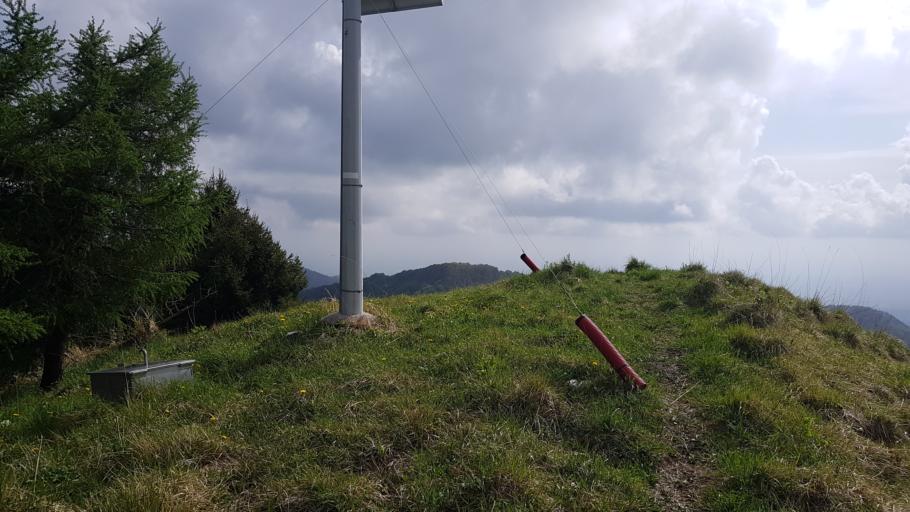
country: IT
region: Friuli Venezia Giulia
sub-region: Provincia di Udine
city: Taipana
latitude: 46.2265
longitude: 13.3558
